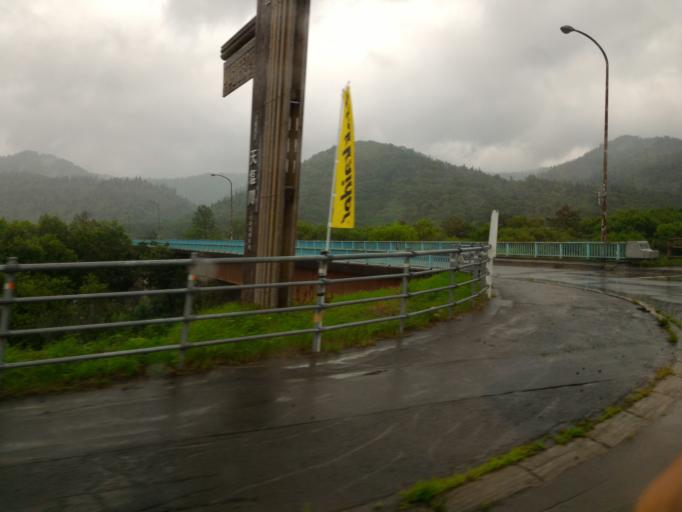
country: JP
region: Hokkaido
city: Nayoro
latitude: 44.7326
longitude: 142.1962
